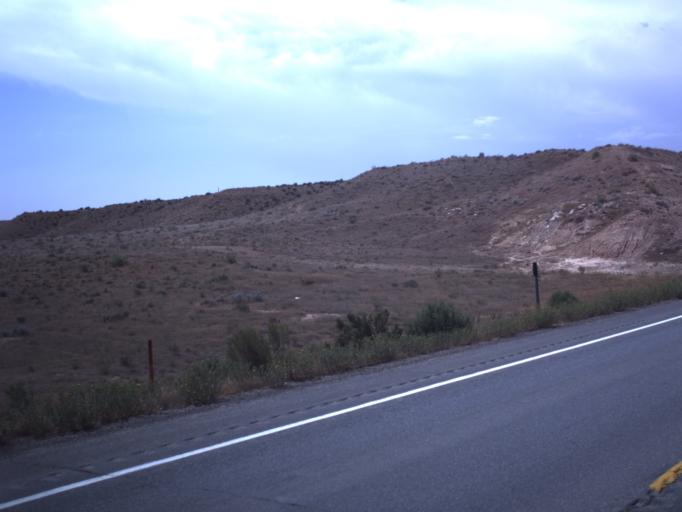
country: US
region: Utah
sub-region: Uintah County
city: Maeser
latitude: 40.3247
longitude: -109.6825
